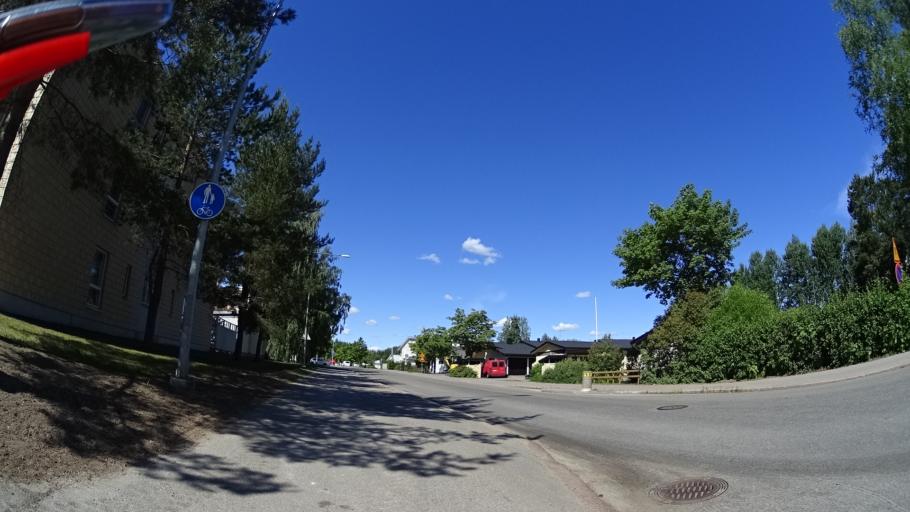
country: FI
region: Uusimaa
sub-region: Helsinki
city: Vantaa
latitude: 60.2973
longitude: 25.0327
